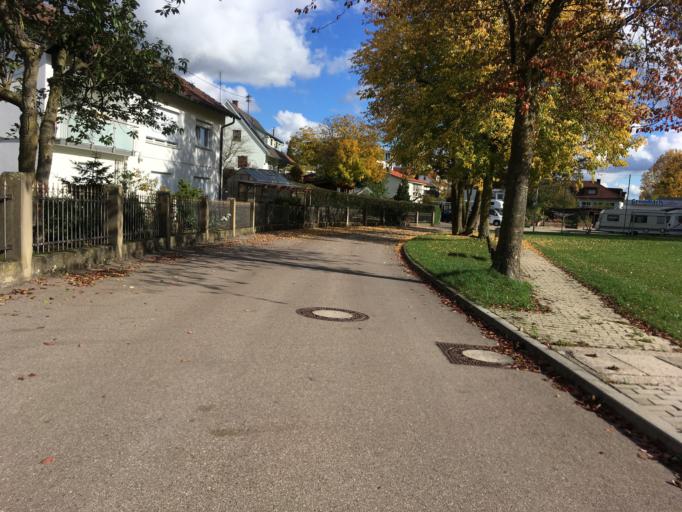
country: DE
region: Baden-Wuerttemberg
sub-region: Regierungsbezirk Stuttgart
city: Waldenburg
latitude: 49.1764
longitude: 9.6793
